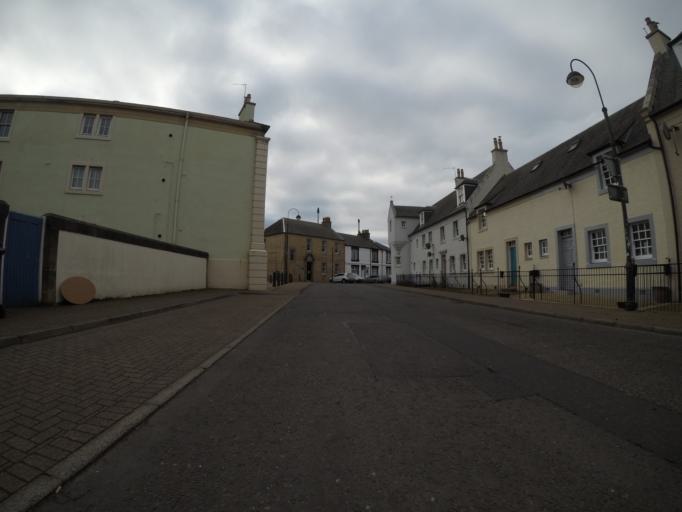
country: GB
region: Scotland
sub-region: North Ayrshire
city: Irvine
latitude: 55.6097
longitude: -4.6783
